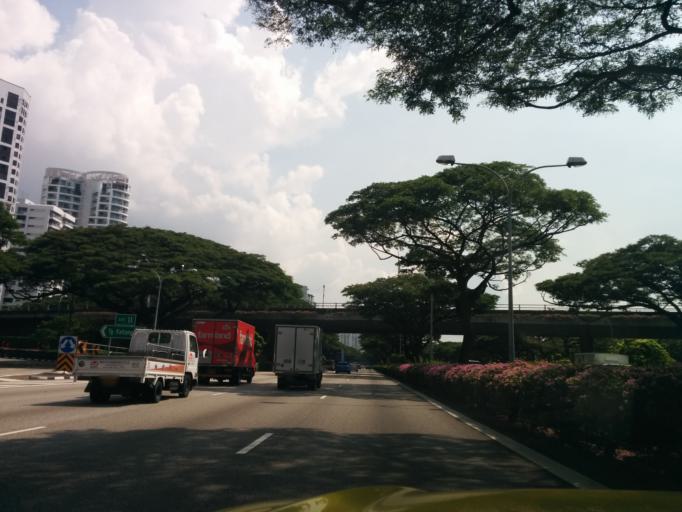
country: SG
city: Singapore
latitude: 1.2971
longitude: 103.8976
